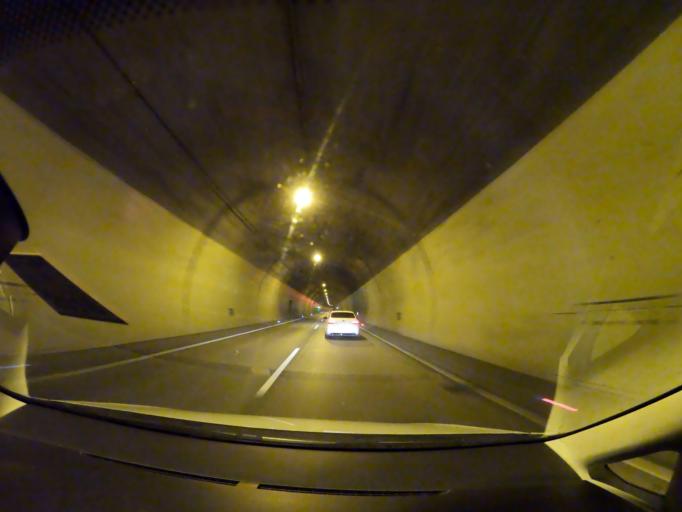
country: AT
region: Styria
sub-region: Politischer Bezirk Voitsberg
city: Modriach
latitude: 46.9725
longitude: 15.0775
